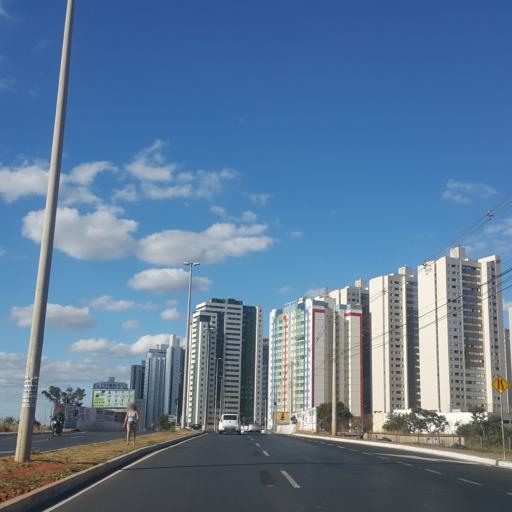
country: BR
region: Federal District
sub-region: Brasilia
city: Brasilia
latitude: -15.8372
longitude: -48.0439
